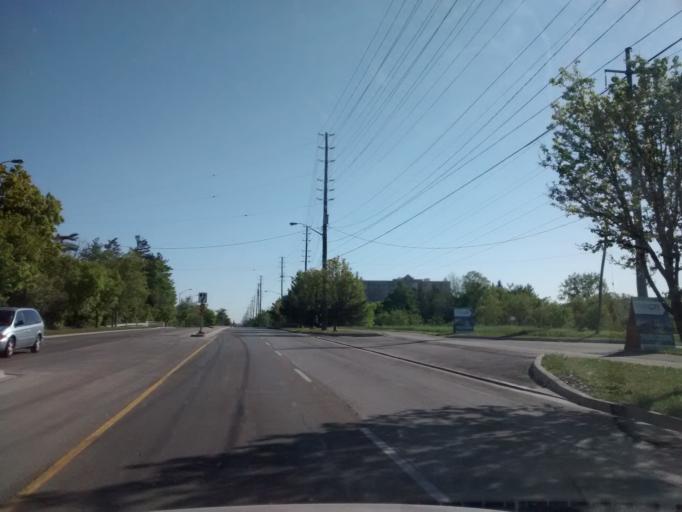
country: CA
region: Ontario
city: Burlington
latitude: 43.3809
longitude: -79.8042
